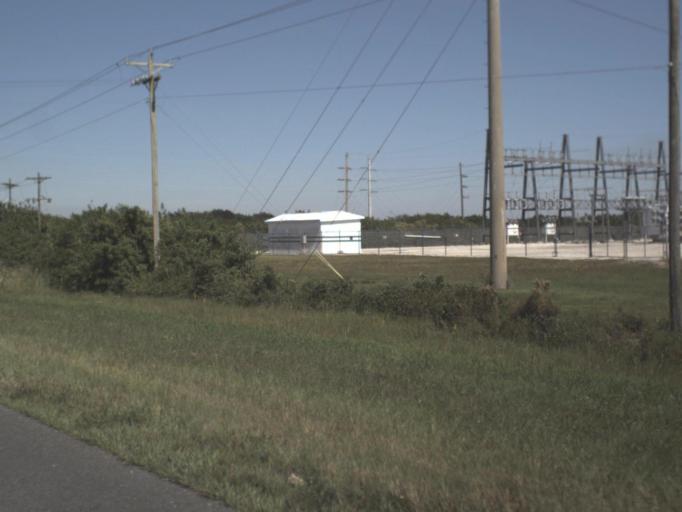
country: US
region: Florida
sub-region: Glades County
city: Moore Haven
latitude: 26.7669
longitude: -81.0829
